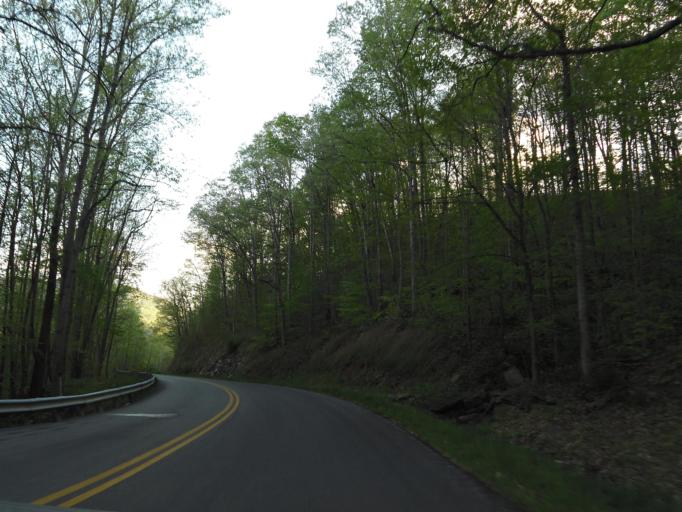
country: US
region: Kentucky
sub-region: Bell County
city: Middlesboro
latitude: 36.6054
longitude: -83.8810
